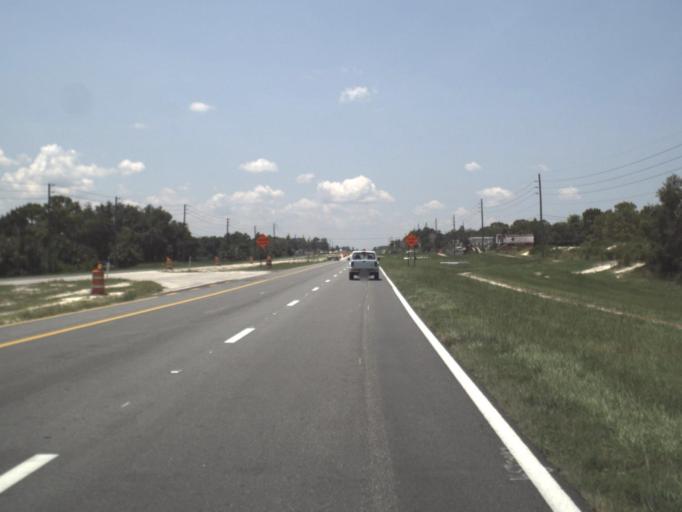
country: US
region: Florida
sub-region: Hernando County
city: North Weeki Wachee
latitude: 28.5519
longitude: -82.5629
